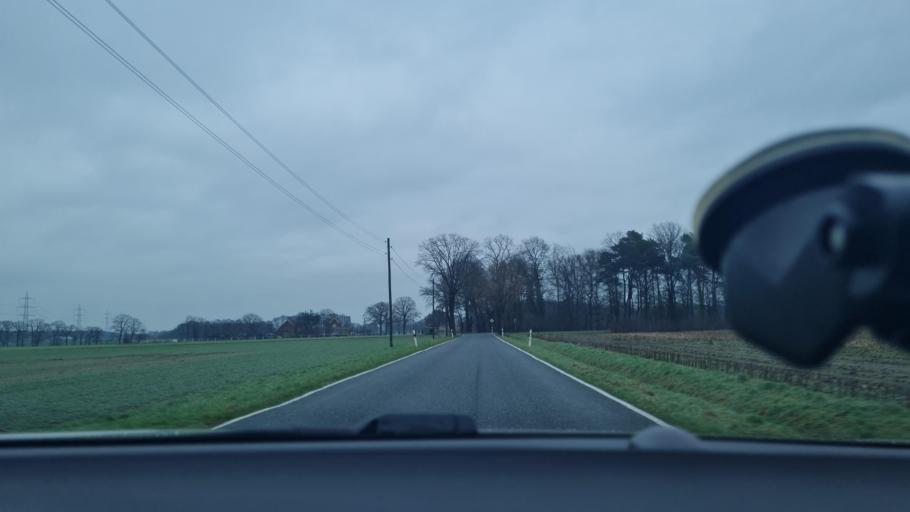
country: DE
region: North Rhine-Westphalia
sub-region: Regierungsbezirk Dusseldorf
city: Hunxe
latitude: 51.7317
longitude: 6.7630
